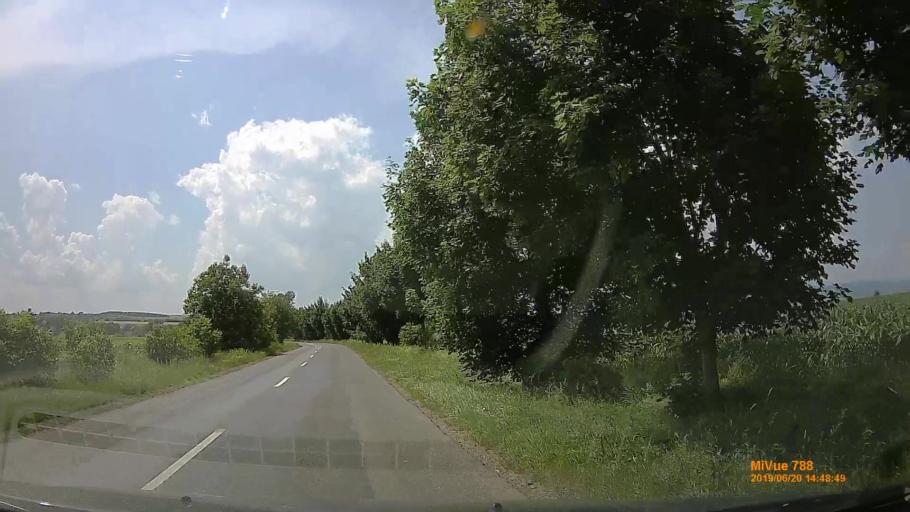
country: HU
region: Baranya
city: Kozarmisleny
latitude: 46.0160
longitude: 18.2830
